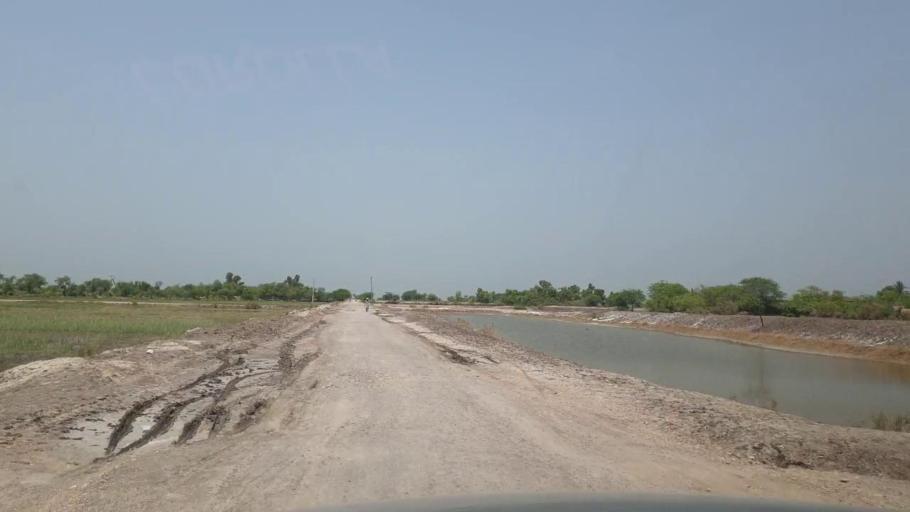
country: PK
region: Sindh
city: Garhi Yasin
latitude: 27.8748
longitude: 68.4460
